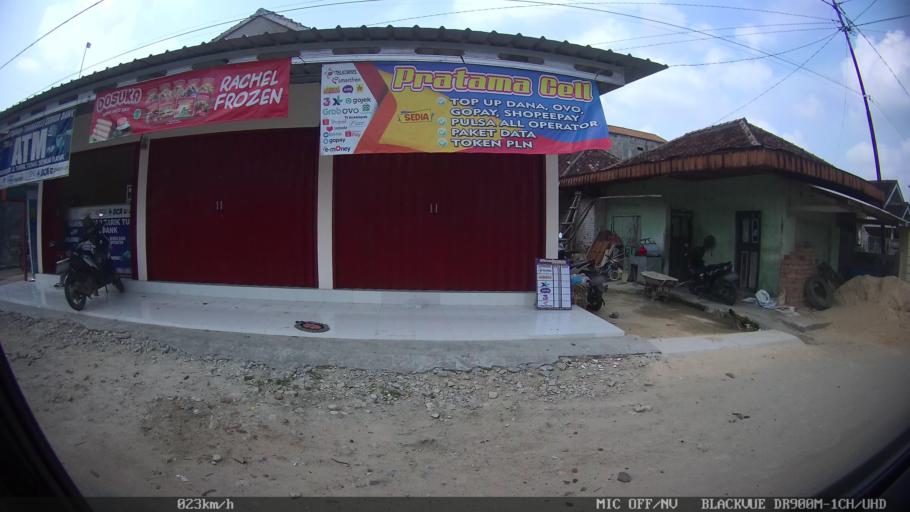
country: ID
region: Lampung
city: Pringsewu
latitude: -5.3578
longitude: 104.9714
